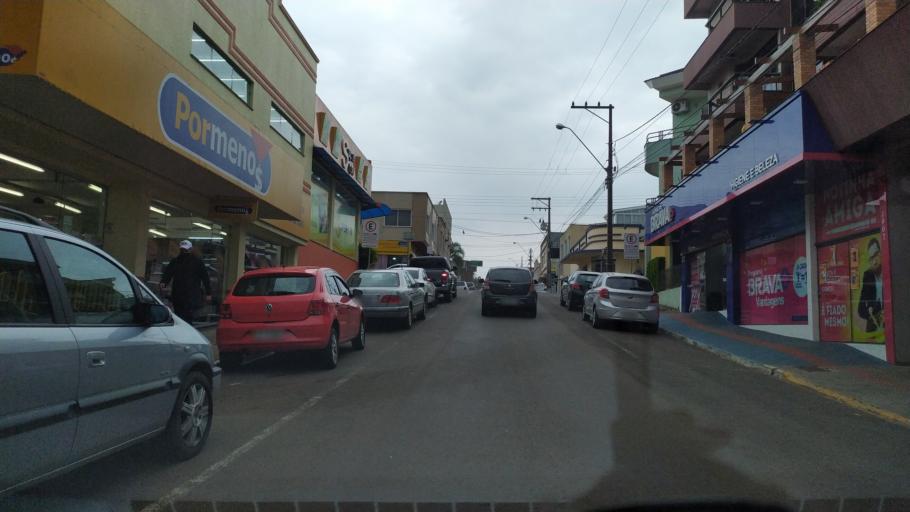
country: BR
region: Parana
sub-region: Palmas
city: Palmas
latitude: -26.4825
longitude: -51.9918
